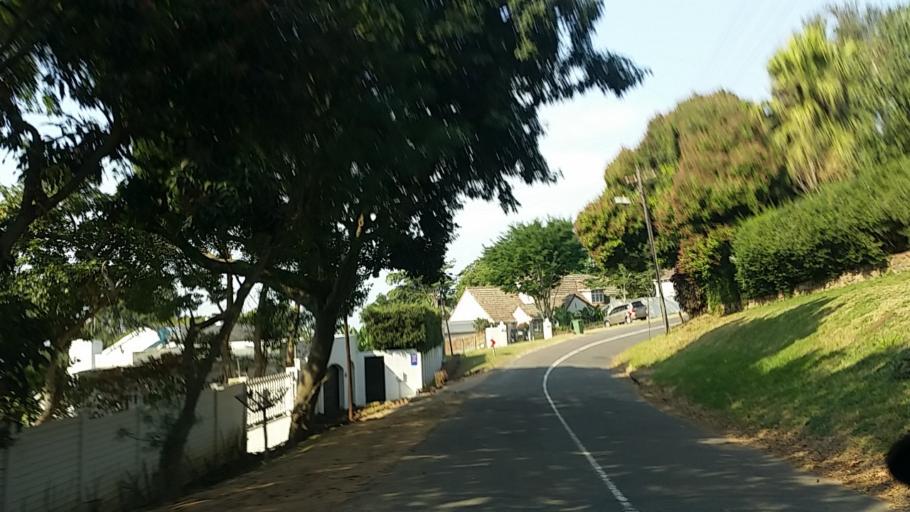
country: ZA
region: KwaZulu-Natal
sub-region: eThekwini Metropolitan Municipality
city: Berea
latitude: -29.8365
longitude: 30.9339
